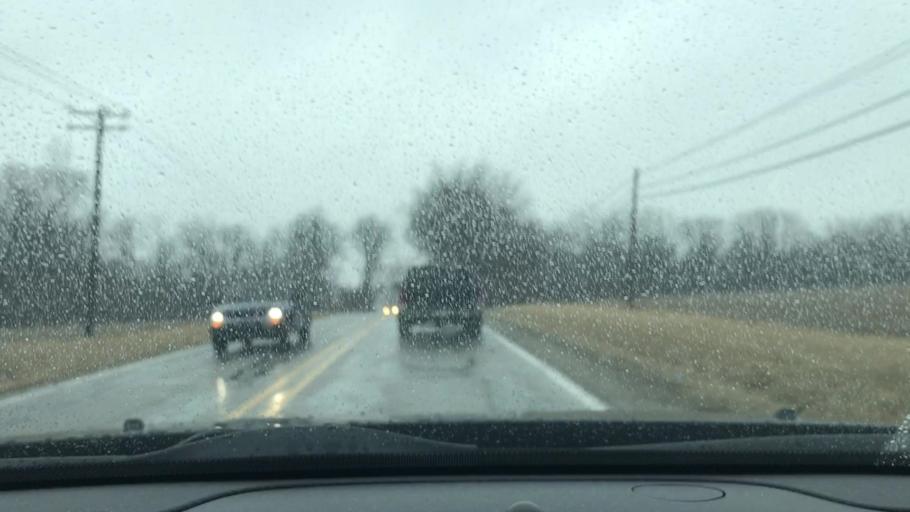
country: US
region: Indiana
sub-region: Morgan County
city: Mooresville
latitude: 39.5953
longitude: -86.3430
